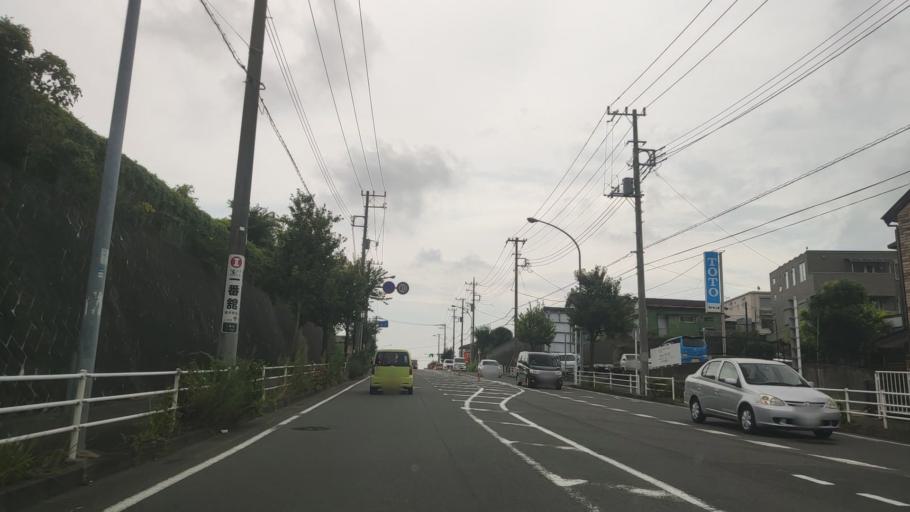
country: JP
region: Kanagawa
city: Minami-rinkan
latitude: 35.4519
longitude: 139.4831
